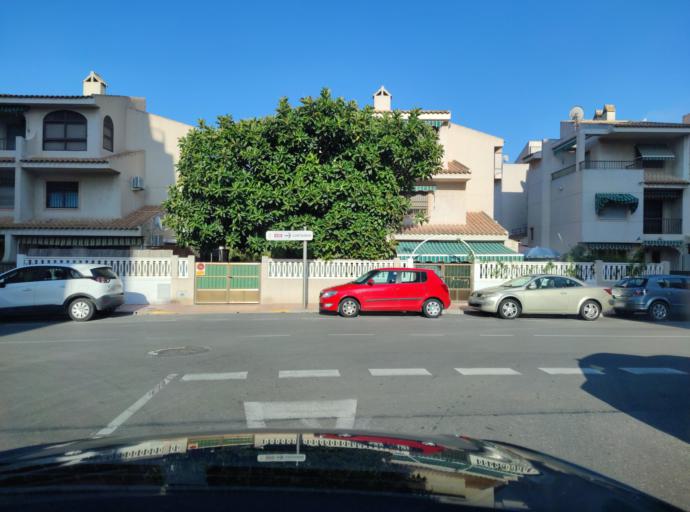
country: ES
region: Valencia
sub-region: Provincia de Alicante
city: Guardamar del Segura
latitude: 38.0826
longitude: -0.6516
